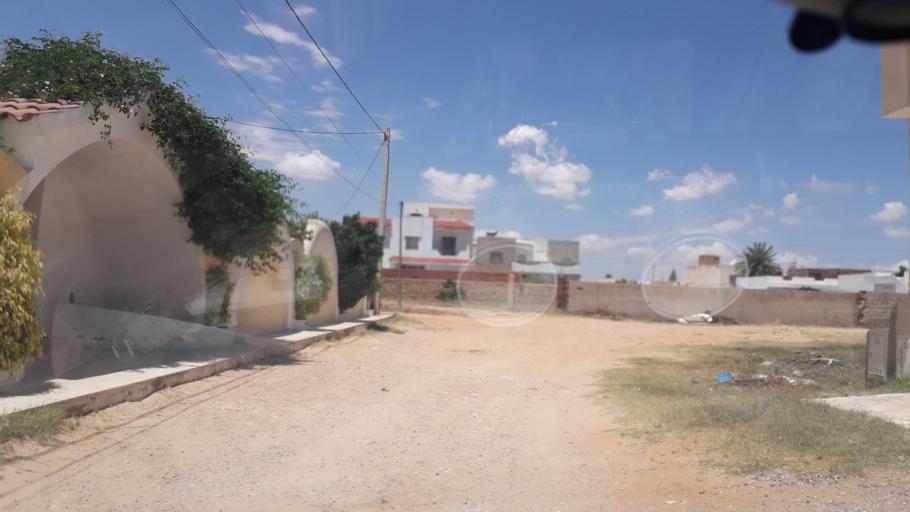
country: TN
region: Safaqis
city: Al Qarmadah
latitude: 34.8190
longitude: 10.7679
